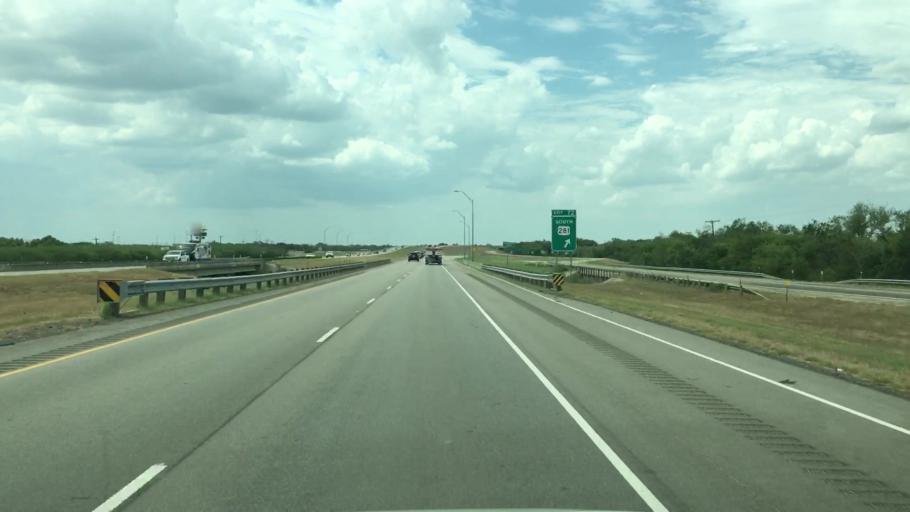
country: US
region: Texas
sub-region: Live Oak County
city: Three Rivers
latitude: 28.5179
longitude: -98.1774
